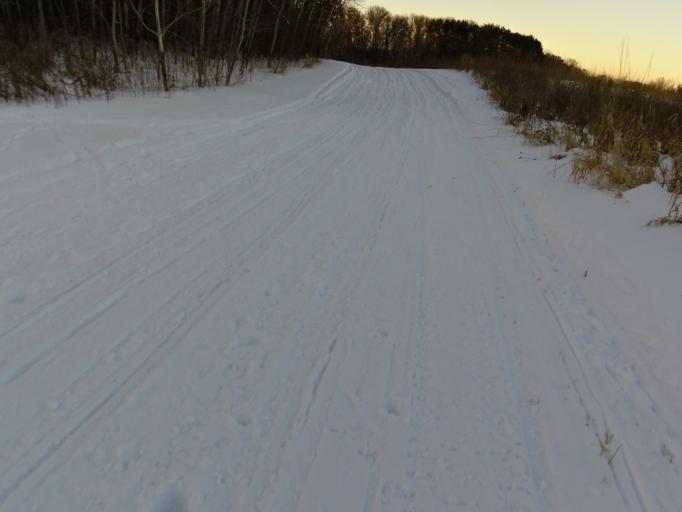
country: US
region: Minnesota
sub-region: Washington County
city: Oakdale
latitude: 44.9739
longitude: -92.9219
